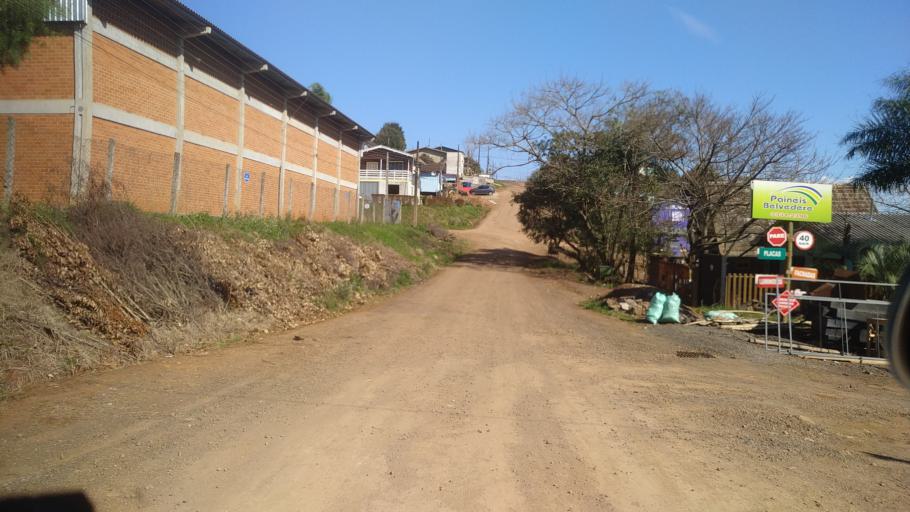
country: BR
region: Santa Catarina
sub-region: Chapeco
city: Chapeco
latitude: -27.0350
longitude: -52.6290
